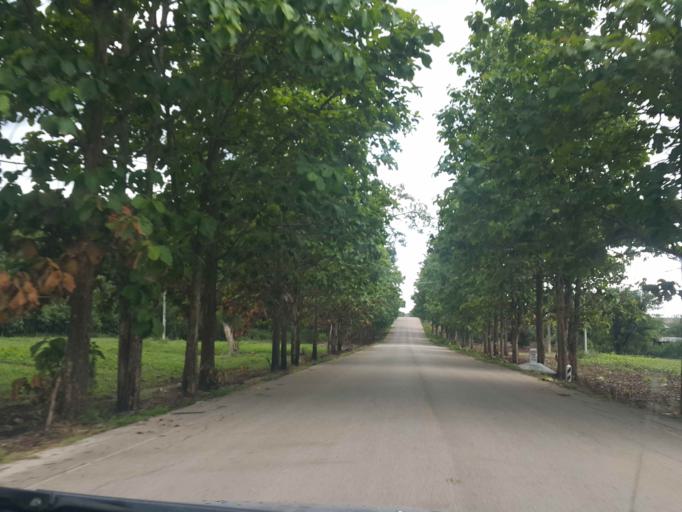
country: TH
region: Phayao
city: Dok Kham Tai
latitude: 18.9802
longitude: 100.0697
